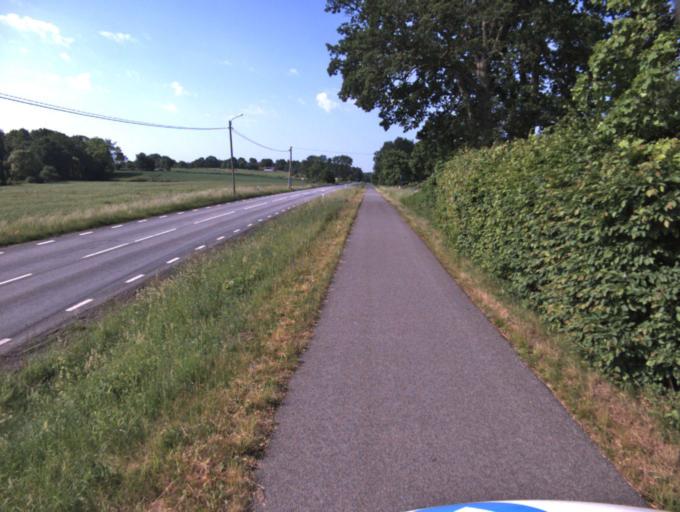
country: SE
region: Skane
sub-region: Kristianstads Kommun
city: Tollarp
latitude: 56.1664
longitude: 14.2805
